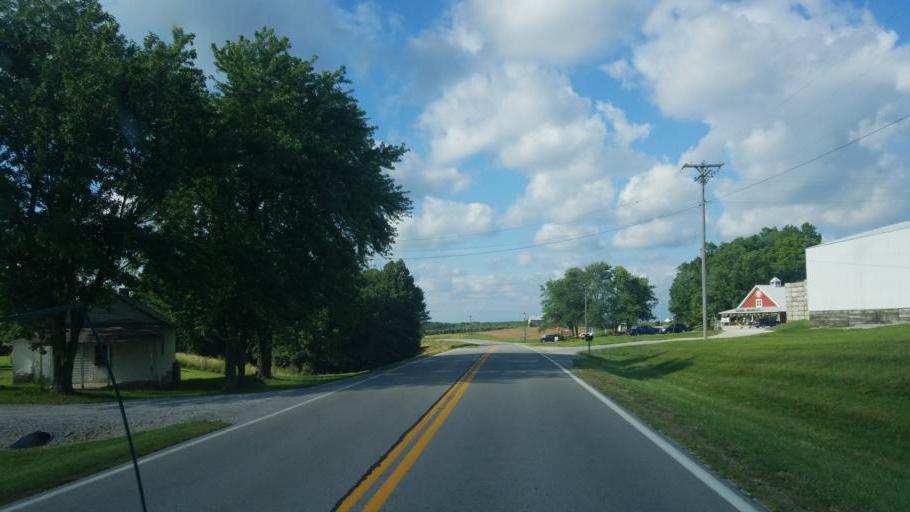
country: US
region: Illinois
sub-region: Union County
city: Cobden
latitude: 37.5941
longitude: -89.3226
